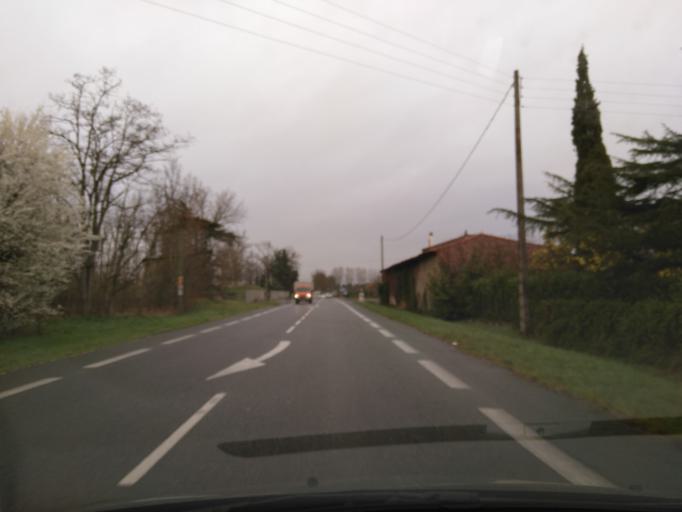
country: FR
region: Midi-Pyrenees
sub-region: Departement de la Haute-Garonne
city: Carbonne
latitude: 43.2871
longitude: 1.2169
